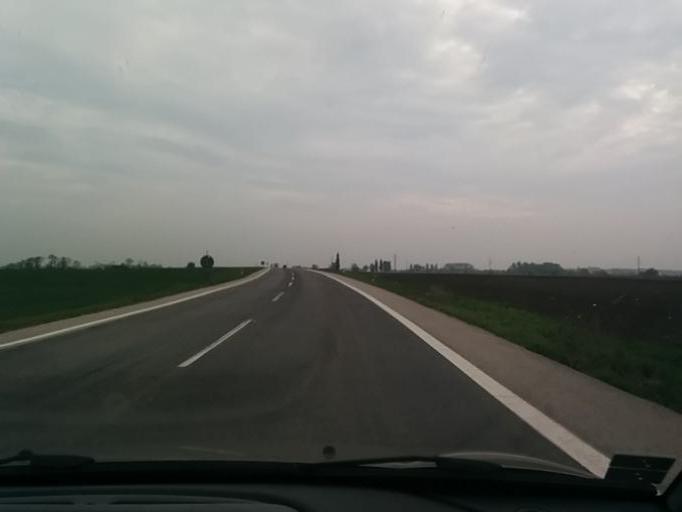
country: SK
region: Trnavsky
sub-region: Okres Galanta
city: Galanta
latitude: 48.2592
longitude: 17.7123
